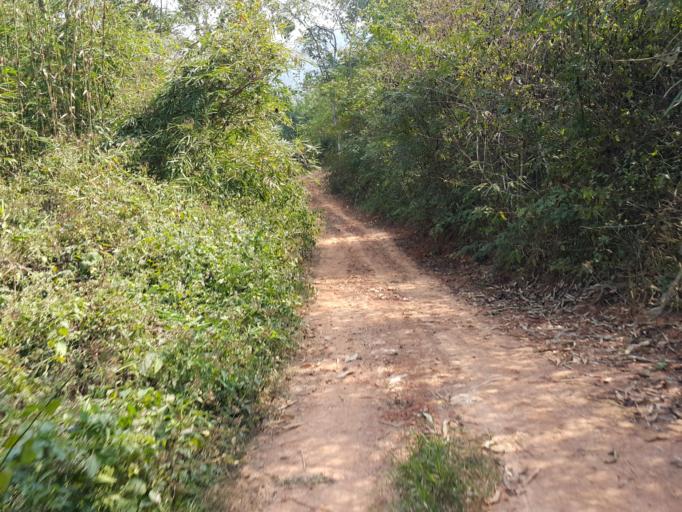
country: TH
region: Sukhothai
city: Thung Saliam
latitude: 17.3260
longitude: 99.4987
